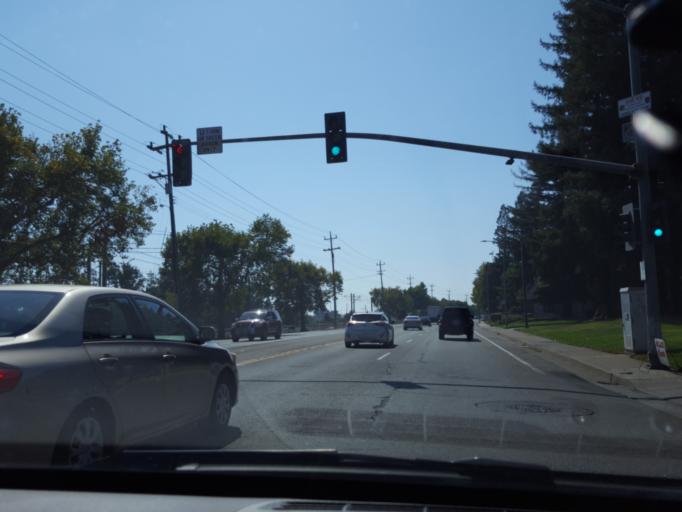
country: US
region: California
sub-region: Sacramento County
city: Rosemont
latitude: 38.5526
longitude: -121.3765
